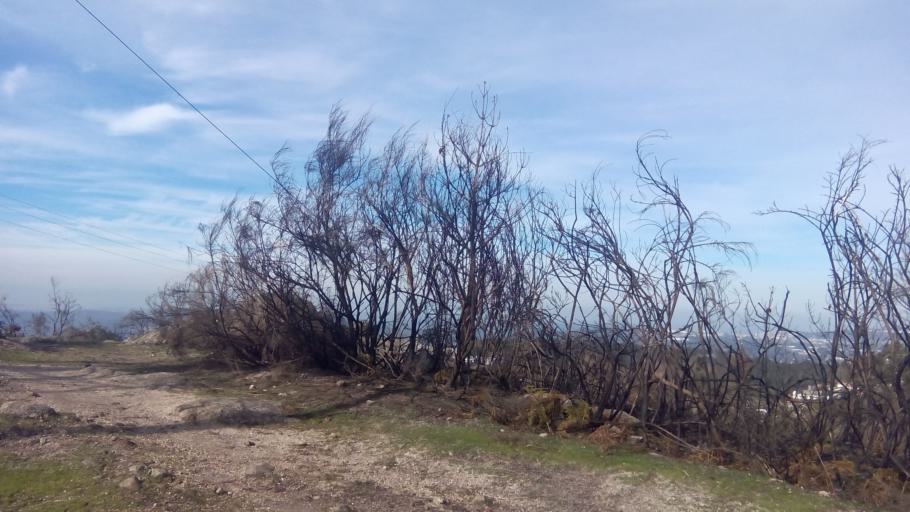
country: PT
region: Porto
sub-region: Paredes
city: Baltar
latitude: 41.2002
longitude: -8.3908
